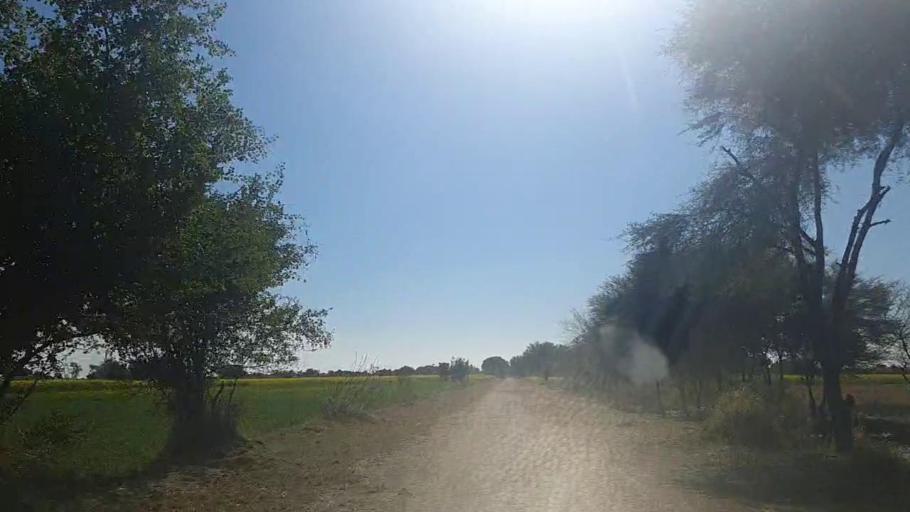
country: PK
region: Sindh
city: Sanghar
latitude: 26.1970
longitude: 68.9105
